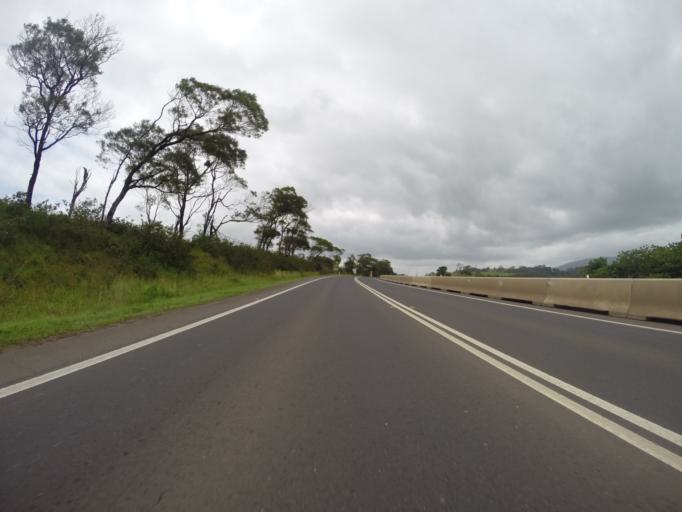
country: AU
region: New South Wales
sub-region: Kiama
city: Gerringong
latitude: -34.7507
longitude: 150.7866
